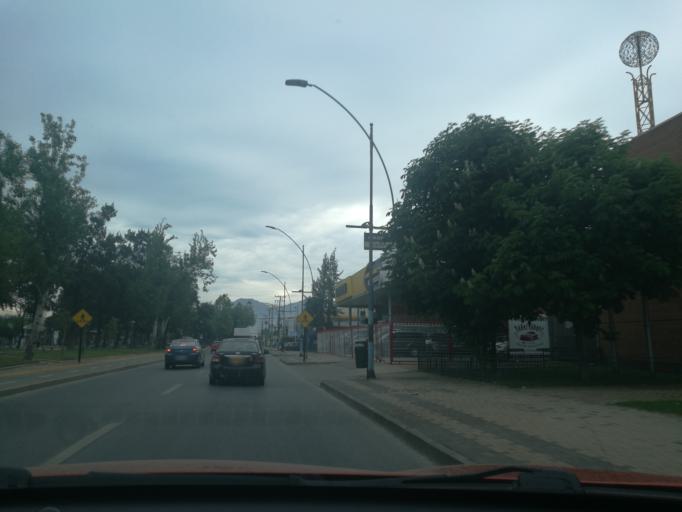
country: CL
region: O'Higgins
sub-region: Provincia de Cachapoal
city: Rancagua
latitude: -34.1666
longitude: -70.7306
